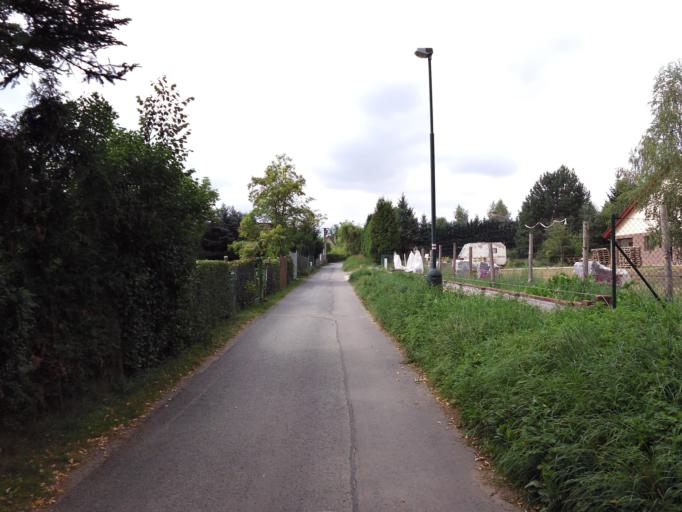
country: CZ
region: Central Bohemia
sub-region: Okres Benesov
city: Cercany
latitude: 49.8722
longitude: 14.7248
